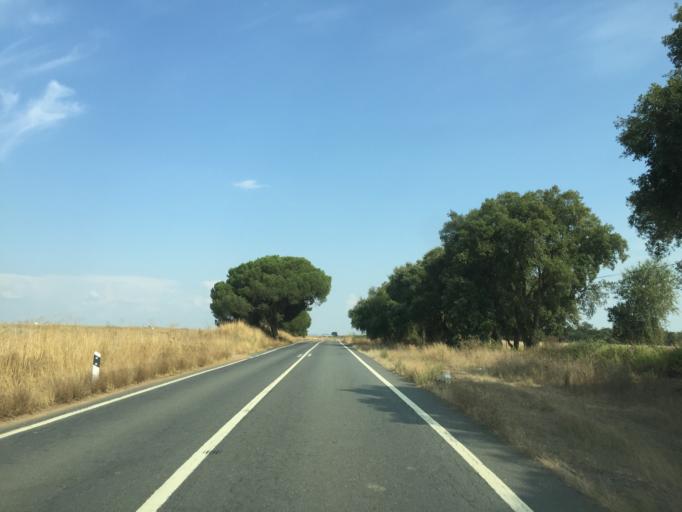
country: PT
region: Beja
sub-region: Aljustrel
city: Aljustrel
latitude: 37.9344
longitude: -8.3546
